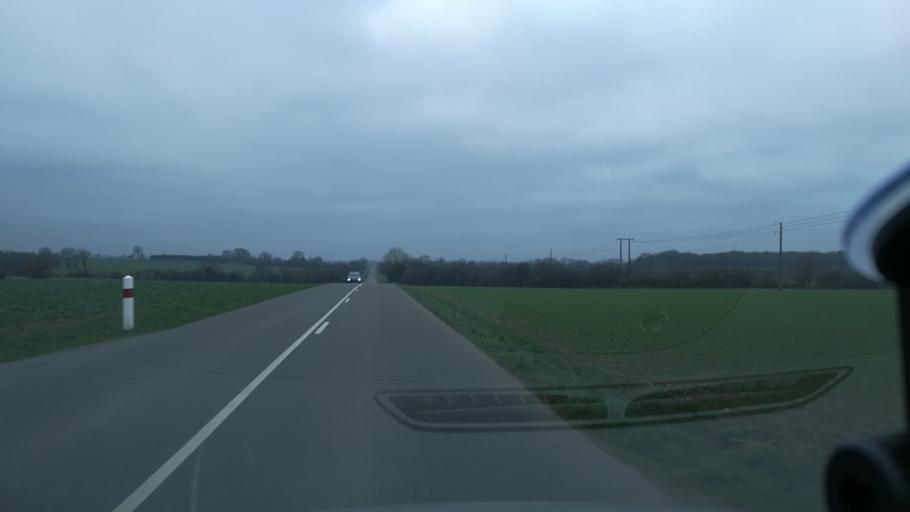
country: FR
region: Brittany
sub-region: Departement d'Ille-et-Vilaine
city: Coesmes
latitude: 47.8853
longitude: -1.4764
